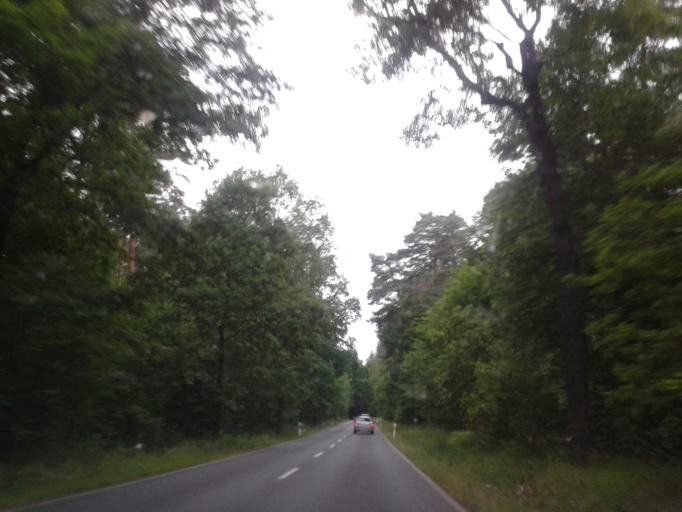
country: DE
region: Saxony
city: Albertstadt
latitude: 51.1022
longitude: 13.7663
